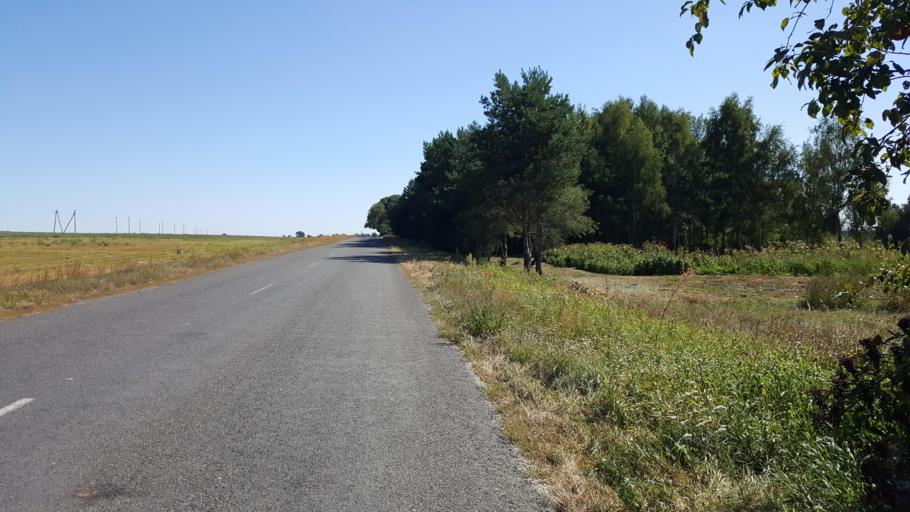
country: PL
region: Lublin Voivodeship
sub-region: Powiat bialski
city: Terespol
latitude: 52.2123
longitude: 23.5180
